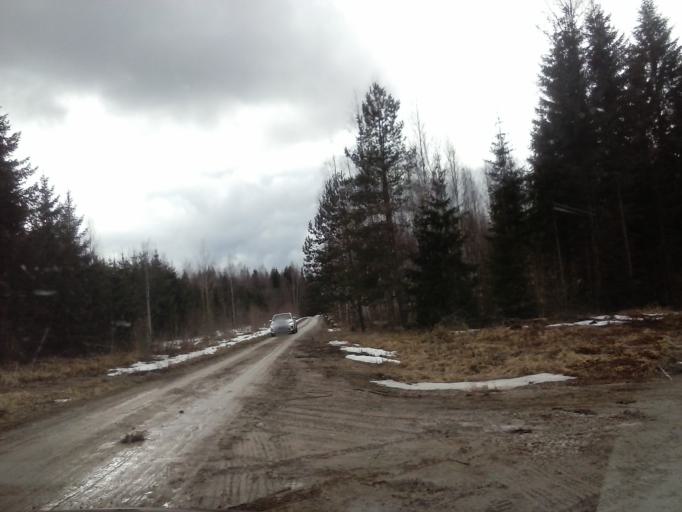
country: EE
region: Ida-Virumaa
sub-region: Johvi vald
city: Johvi
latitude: 59.1823
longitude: 27.3392
